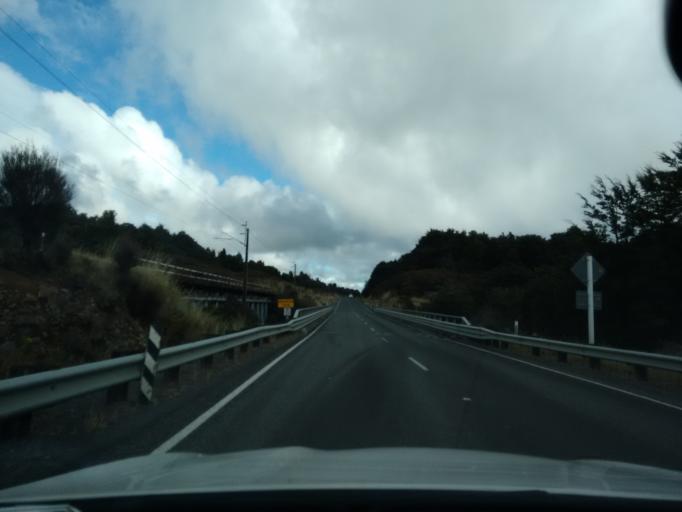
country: NZ
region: Manawatu-Wanganui
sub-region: Ruapehu District
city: Waiouru
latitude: -39.3042
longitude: 175.3898
